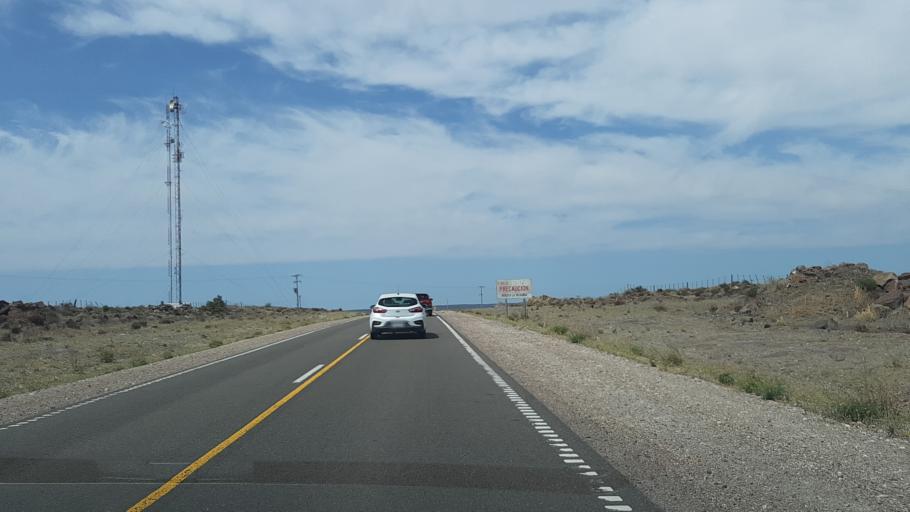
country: AR
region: Neuquen
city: Piedra del Aguila
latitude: -39.9967
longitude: -70.0424
